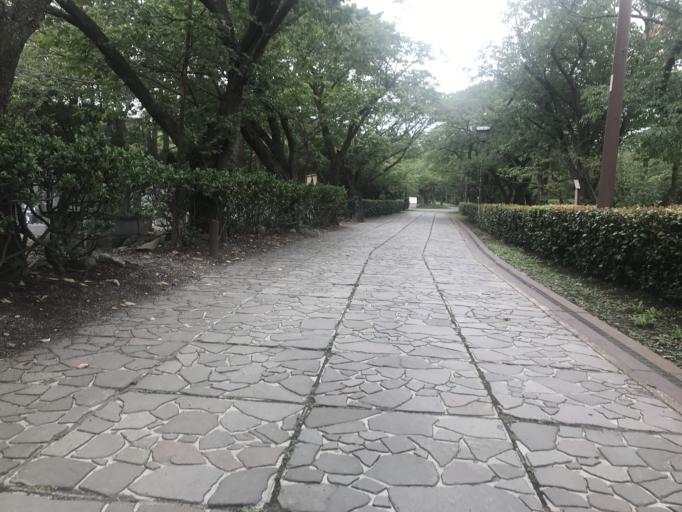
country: JP
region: Hokkaido
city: Kamiiso
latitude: 41.4317
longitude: 140.1088
